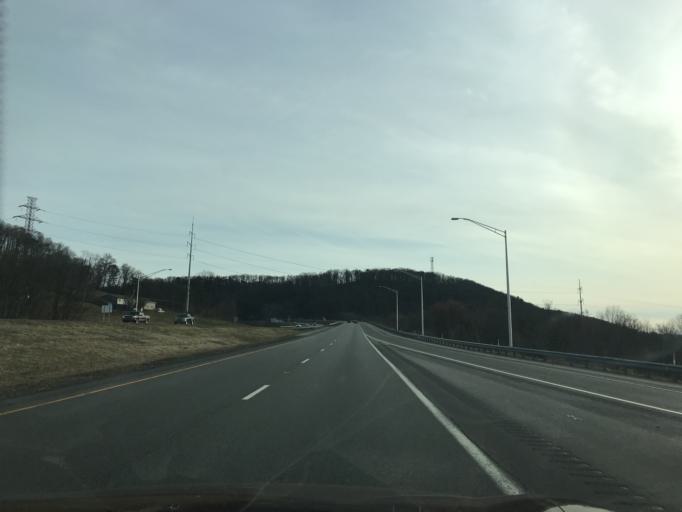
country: US
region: Pennsylvania
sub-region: Lycoming County
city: Muncy
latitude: 41.1864
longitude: -76.7878
